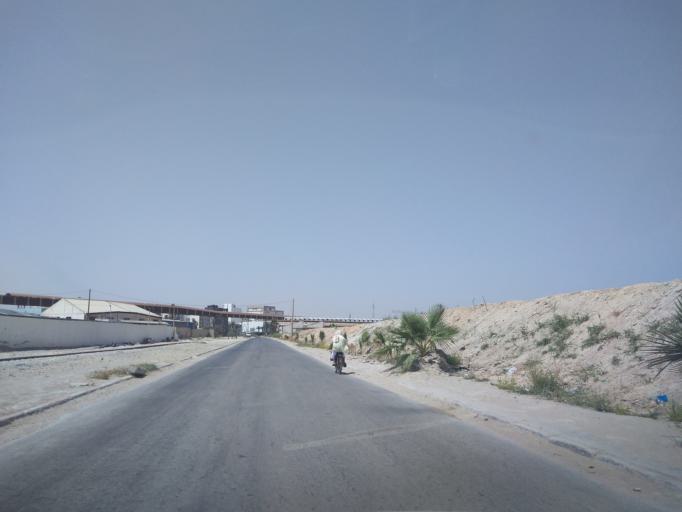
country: TN
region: Safaqis
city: Sfax
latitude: 34.7324
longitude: 10.7741
